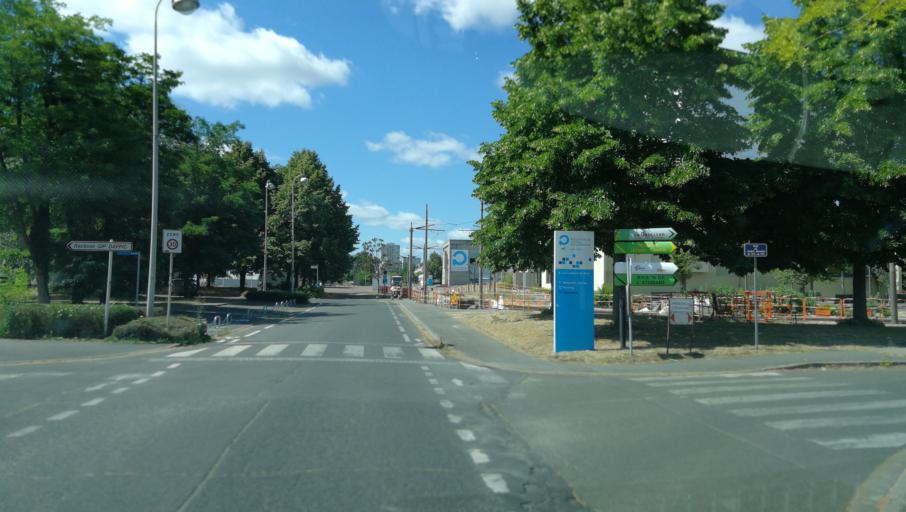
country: FR
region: Centre
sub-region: Departement du Loiret
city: Saint-Cyr-en-Val
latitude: 47.8448
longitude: 1.9398
